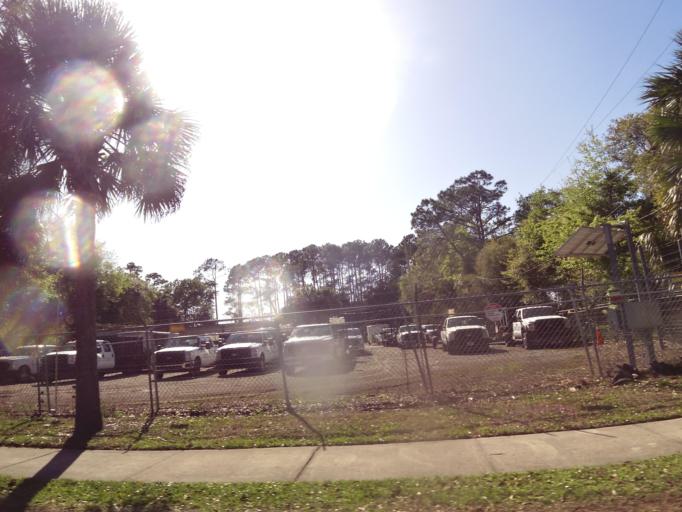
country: US
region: Florida
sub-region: Duval County
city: Jacksonville
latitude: 30.2884
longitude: -81.5874
